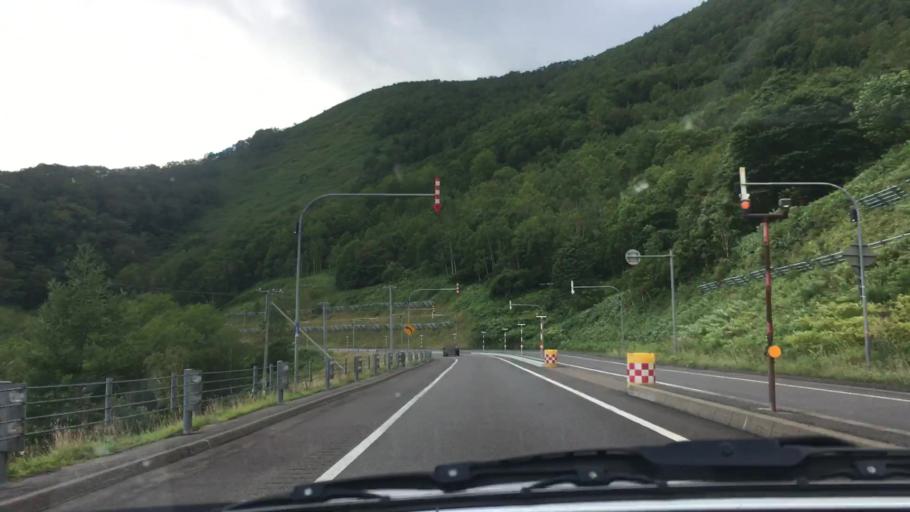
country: JP
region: Hokkaido
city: Shimo-furano
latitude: 43.1524
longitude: 142.7762
